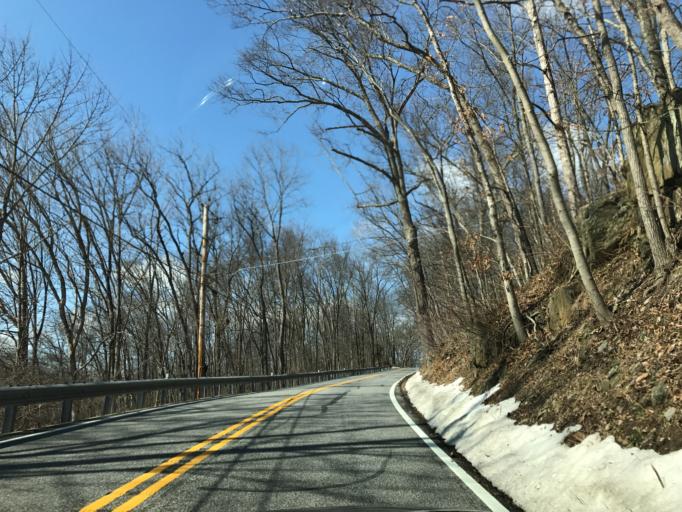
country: US
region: Maryland
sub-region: Carroll County
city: Hampstead
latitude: 39.5831
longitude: -76.7636
